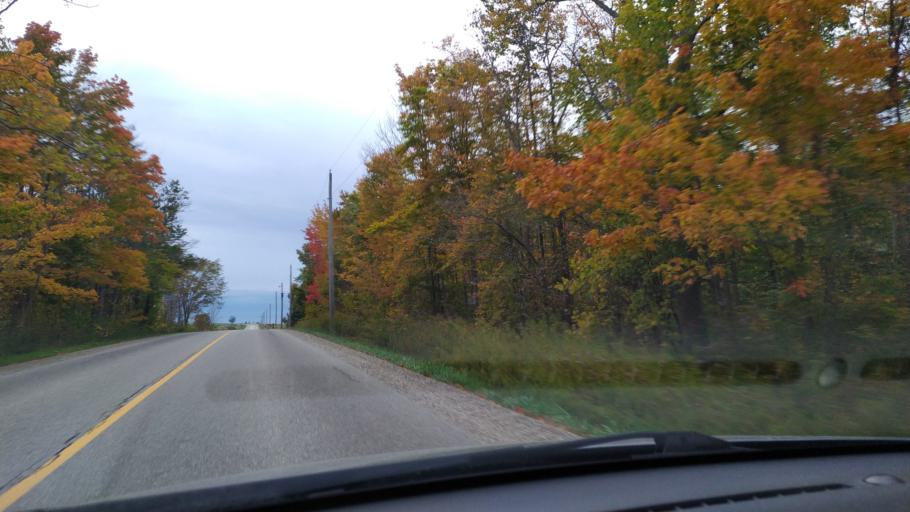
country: CA
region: Ontario
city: Waterloo
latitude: 43.5130
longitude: -80.7464
